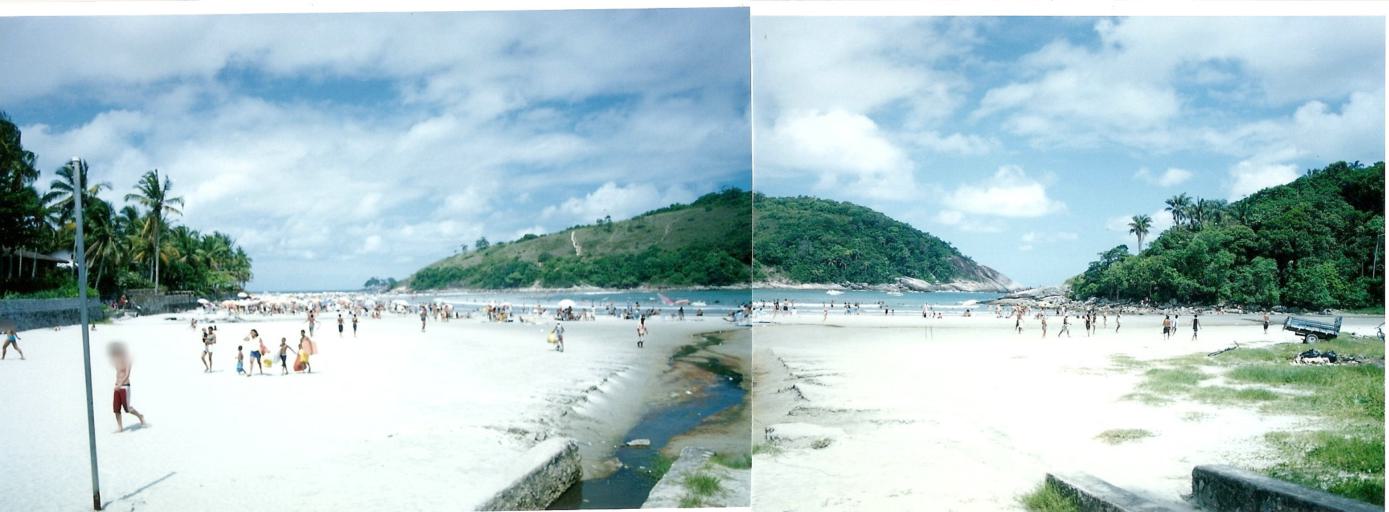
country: BR
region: Sao Paulo
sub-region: Guaruja
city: Guaruja
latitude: -23.9724
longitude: -46.1882
